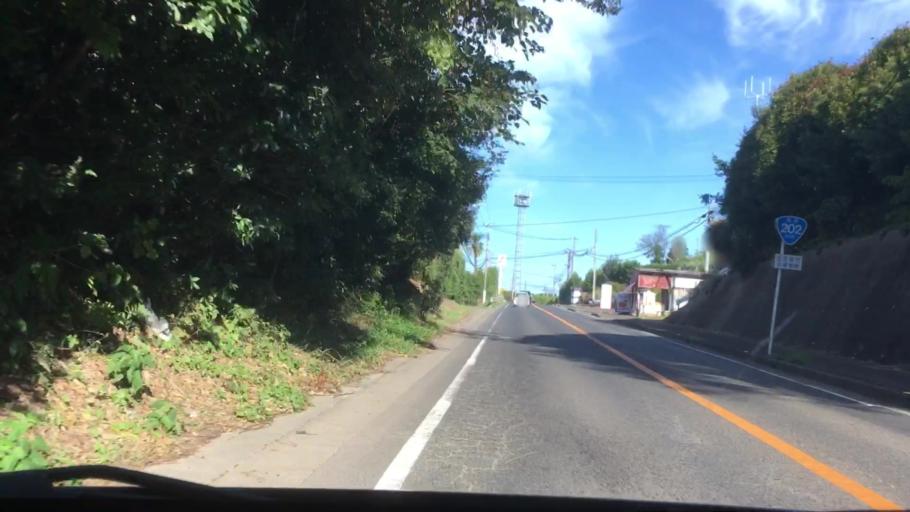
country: JP
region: Nagasaki
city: Sasebo
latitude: 33.0698
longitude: 129.7626
